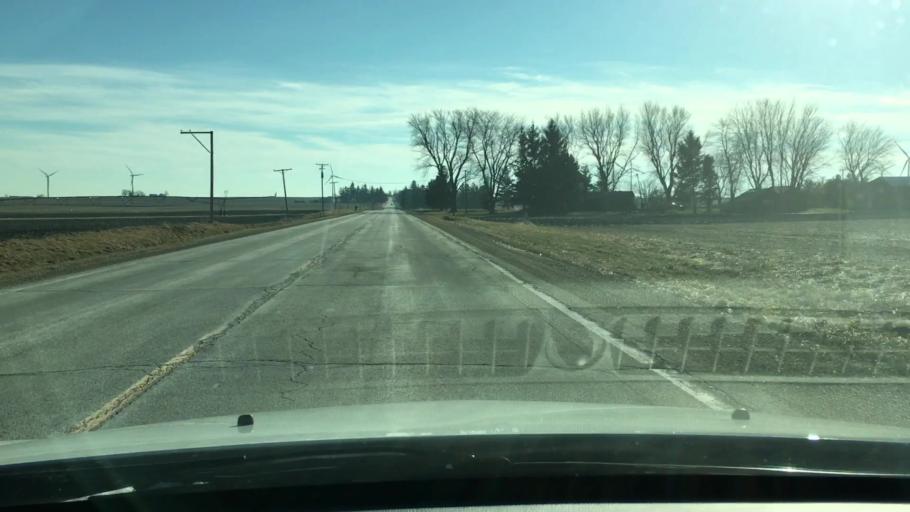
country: US
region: Illinois
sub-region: LaSalle County
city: Mendota
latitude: 41.6474
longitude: -89.1296
